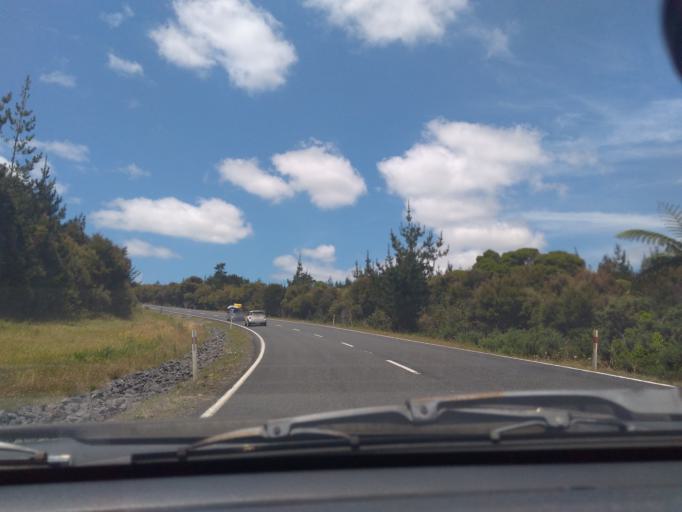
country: NZ
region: Northland
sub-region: Far North District
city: Kerikeri
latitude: -35.1221
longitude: 173.8471
